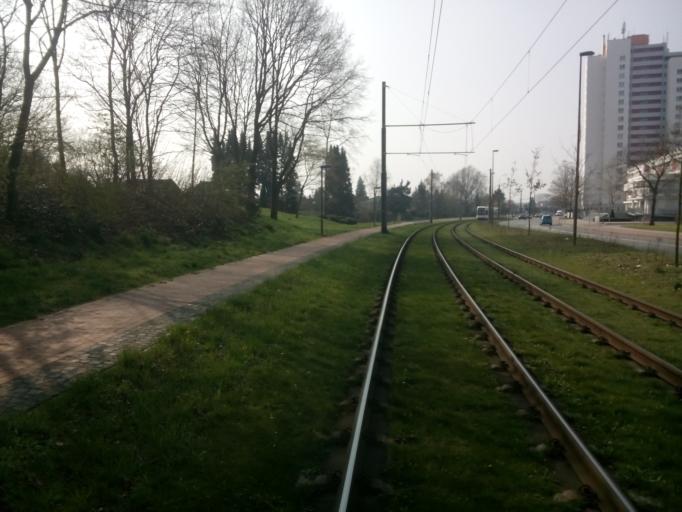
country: DE
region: Lower Saxony
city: Oyten
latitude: 53.0630
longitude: 8.9646
